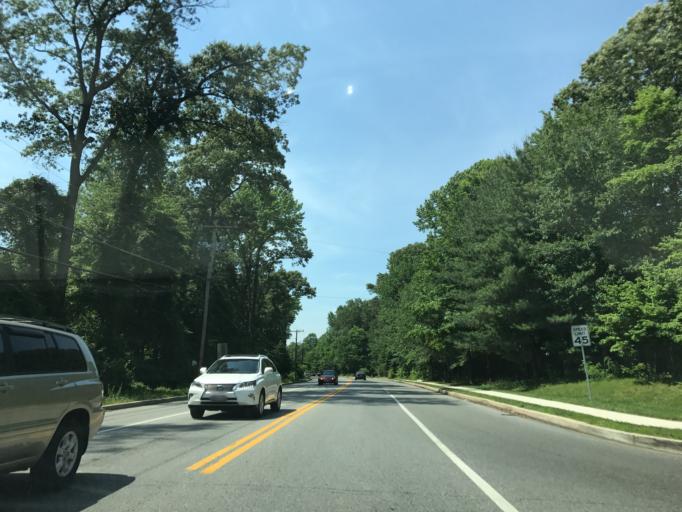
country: US
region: Maryland
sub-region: Anne Arundel County
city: Crofton
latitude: 39.0119
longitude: -76.6826
